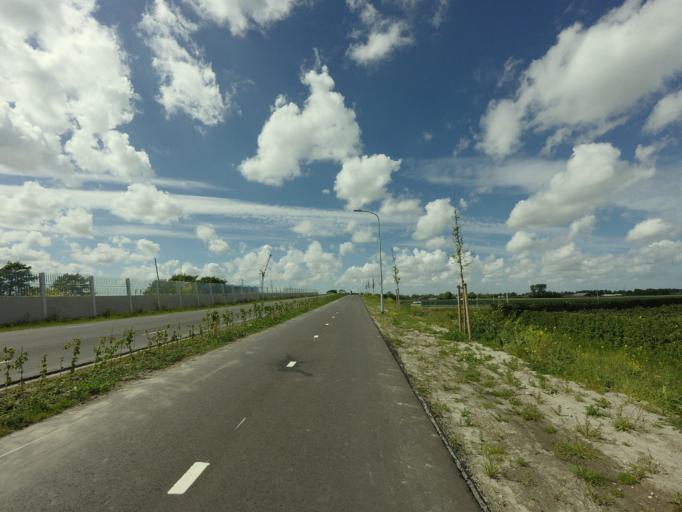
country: NL
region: North Holland
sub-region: Gemeente Hoorn
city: Hoorn
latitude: 52.6797
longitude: 5.0907
